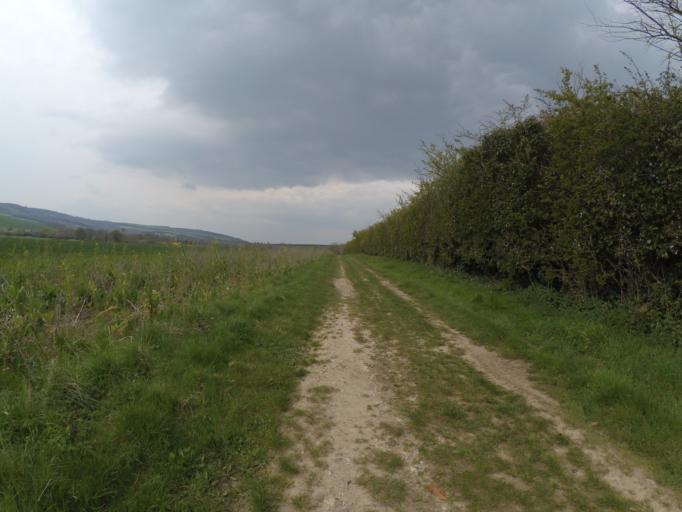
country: GB
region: England
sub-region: West Sussex
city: Arundel
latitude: 50.8767
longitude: -0.5295
